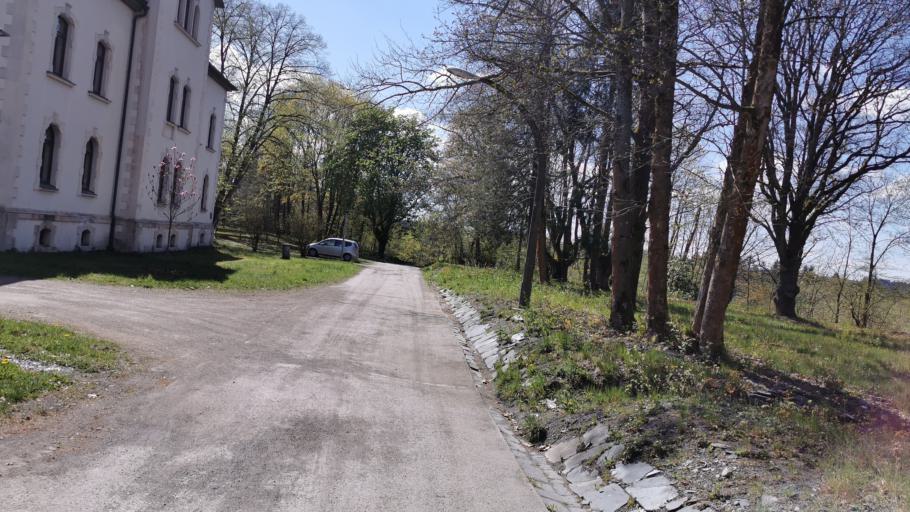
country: DE
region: Bavaria
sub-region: Upper Franconia
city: Reichenbach
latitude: 50.4625
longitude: 11.4366
